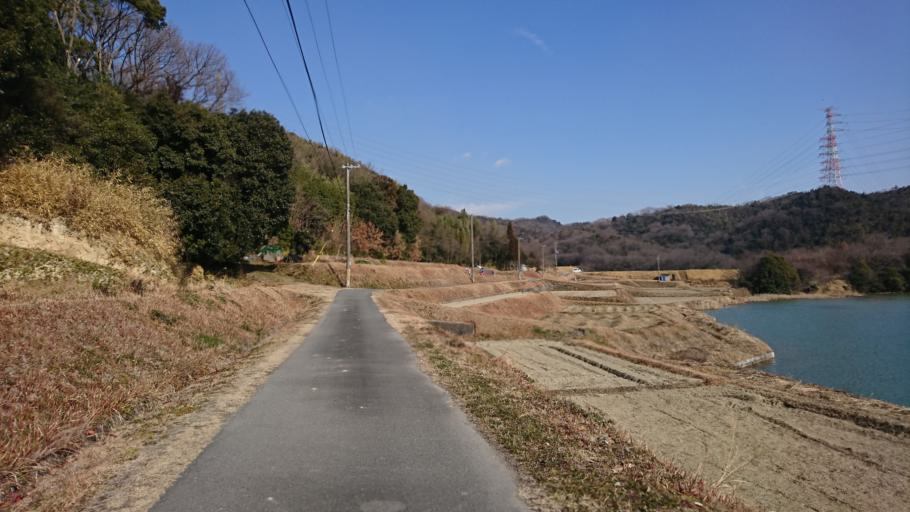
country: JP
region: Hyogo
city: Kakogawacho-honmachi
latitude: 34.8206
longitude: 134.8556
